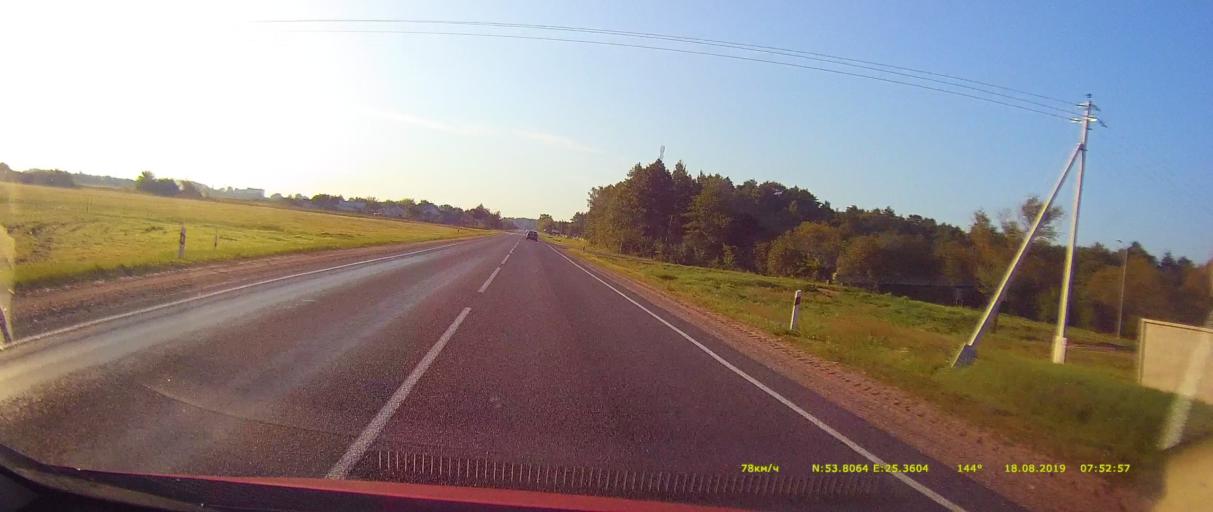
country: BY
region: Grodnenskaya
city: Dzyatlava
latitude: 53.3257
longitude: 25.2772
